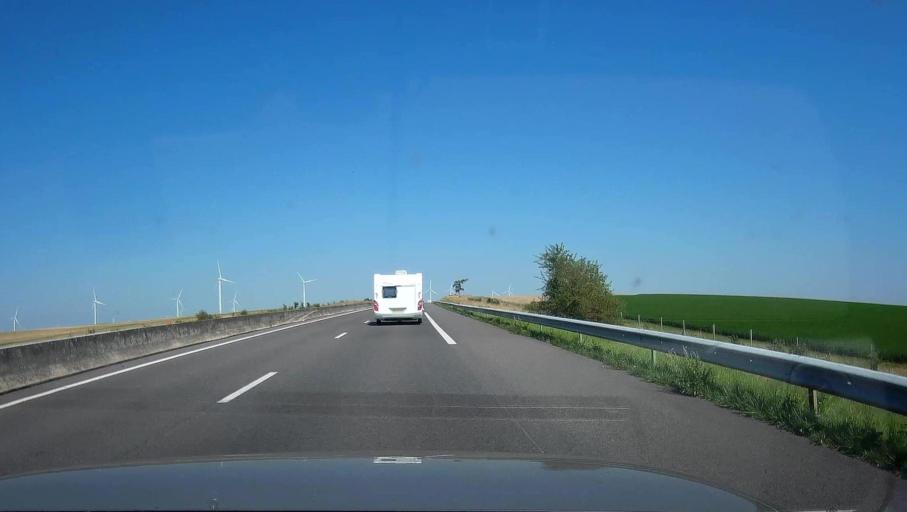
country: FR
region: Champagne-Ardenne
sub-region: Departement de l'Aube
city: Mailly-le-Camp
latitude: 48.6048
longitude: 4.1798
